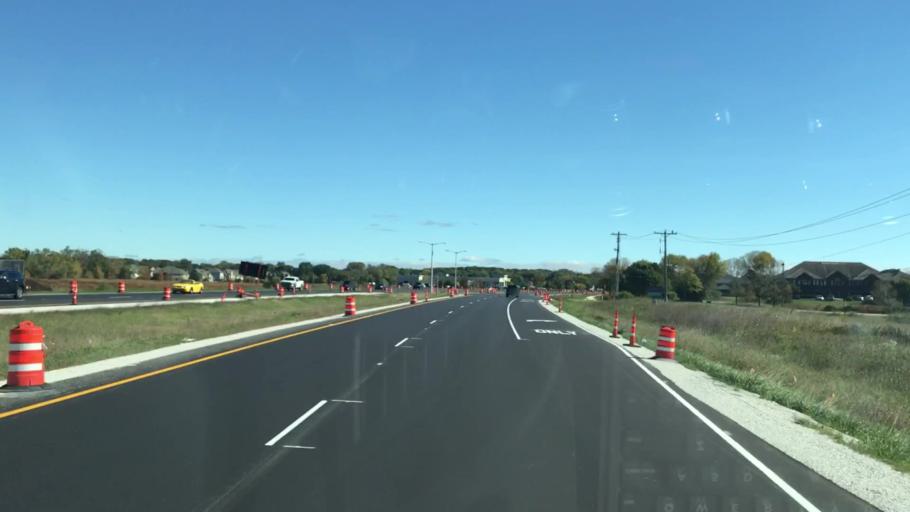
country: US
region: Wisconsin
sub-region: Waukesha County
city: Lannon
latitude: 43.0899
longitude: -88.1579
